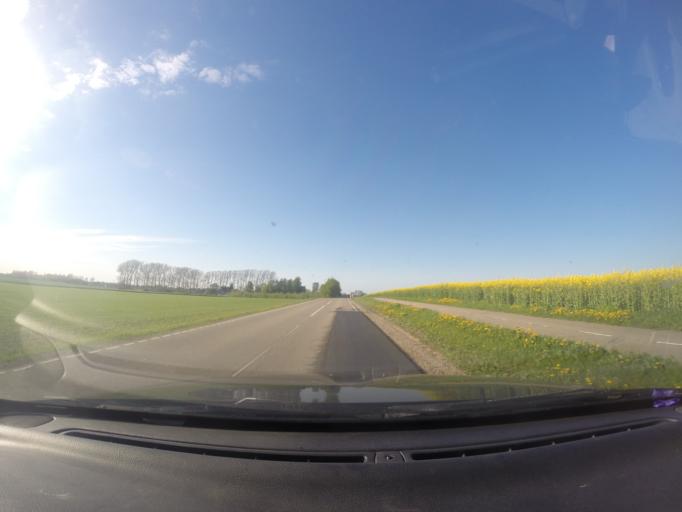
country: DK
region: Capital Region
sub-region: Hoje-Taastrup Kommune
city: Taastrup
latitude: 55.6748
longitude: 12.2538
